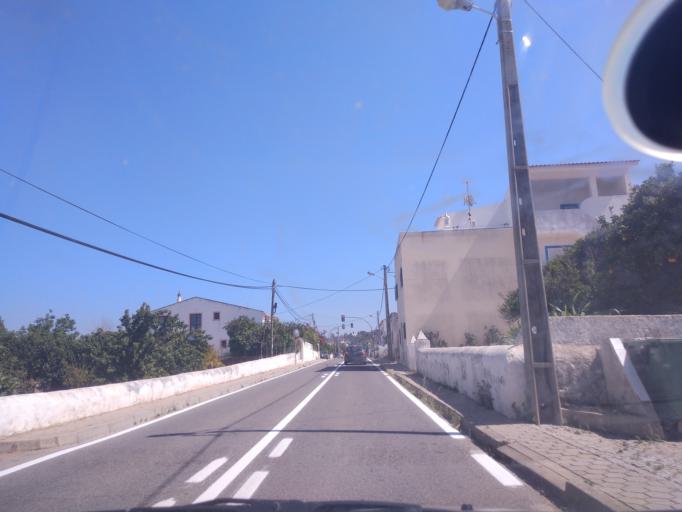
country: PT
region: Faro
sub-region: Lagos
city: Lagos
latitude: 37.1247
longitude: -8.6951
